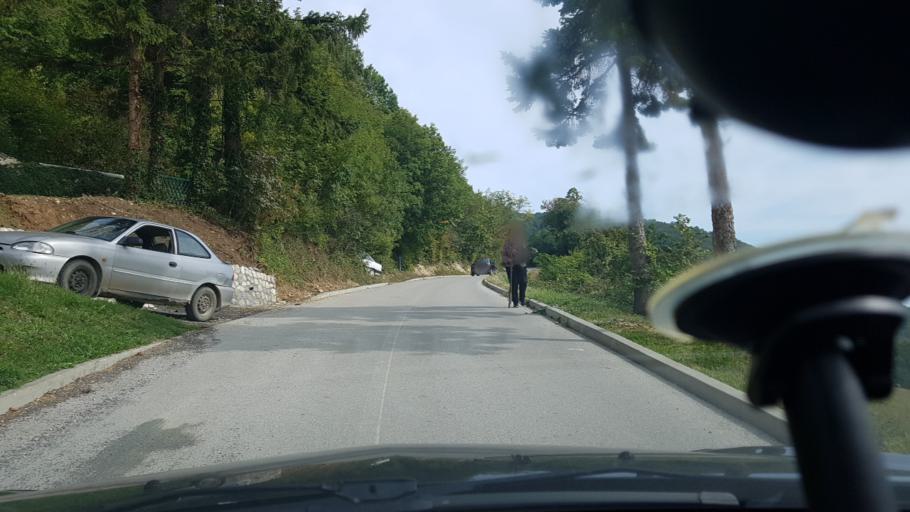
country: HR
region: Varazdinska
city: Ljubescica
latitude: 46.1291
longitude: 16.4626
